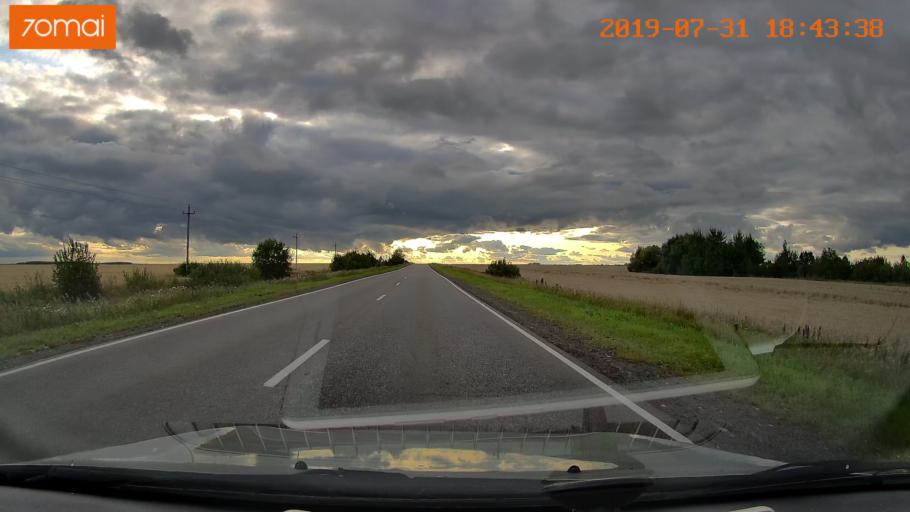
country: RU
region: Moskovskaya
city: Troitskoye
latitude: 55.2456
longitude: 38.5714
